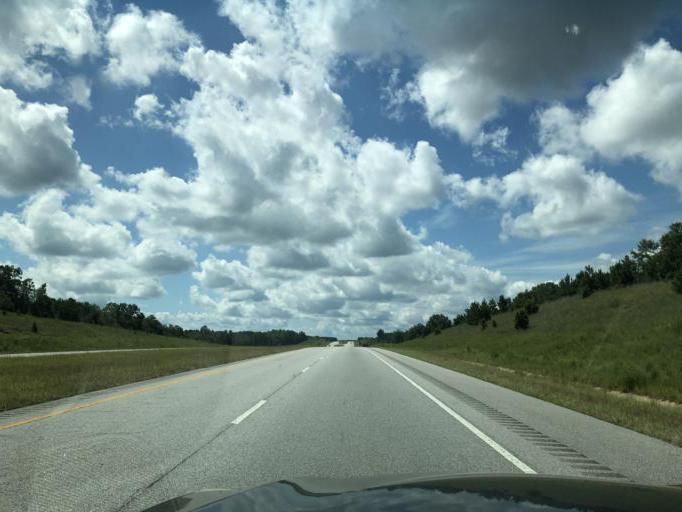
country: US
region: Alabama
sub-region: Barbour County
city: Eufaula
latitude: 32.1073
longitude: -85.1503
